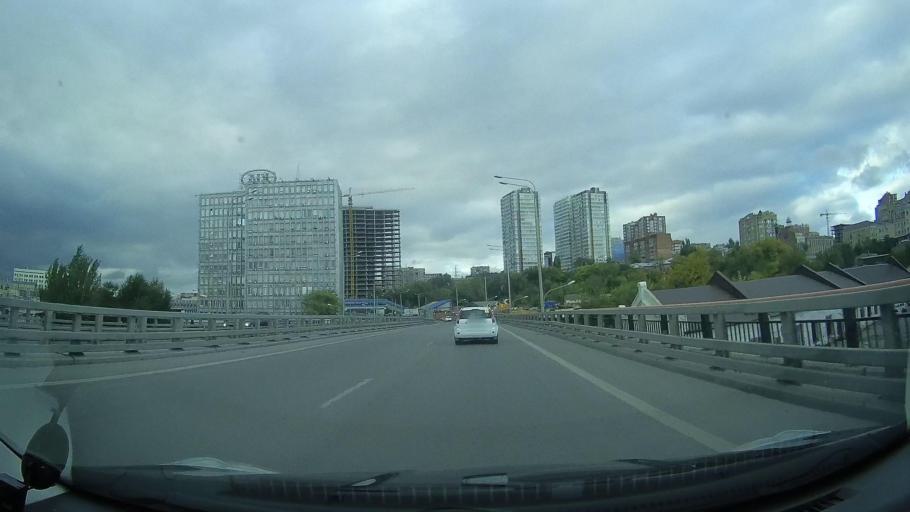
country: RU
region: Rostov
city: Rostov-na-Donu
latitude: 47.2186
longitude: 39.6946
